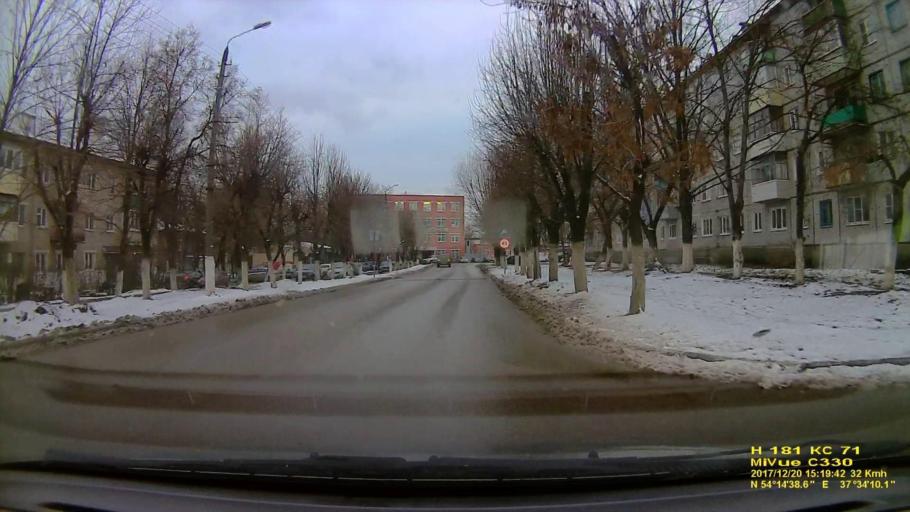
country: RU
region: Tula
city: Gorelki
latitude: 54.2440
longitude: 37.5694
